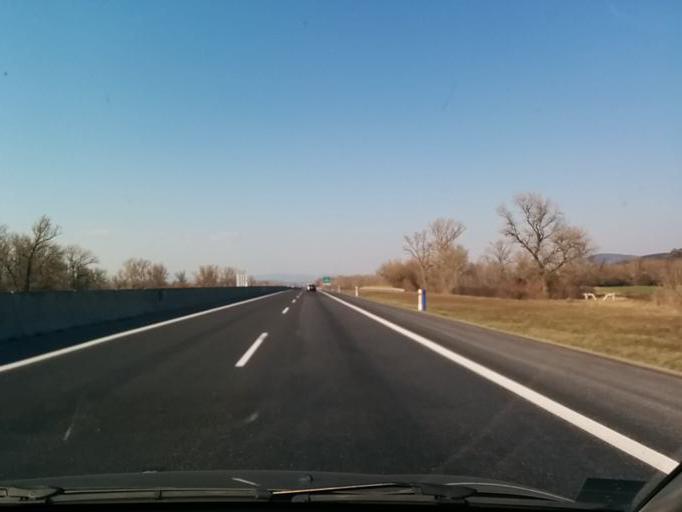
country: SK
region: Trenciansky
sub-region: Okres Nove Mesto nad Vahom
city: Nove Mesto nad Vahom
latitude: 48.6803
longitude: 17.8728
